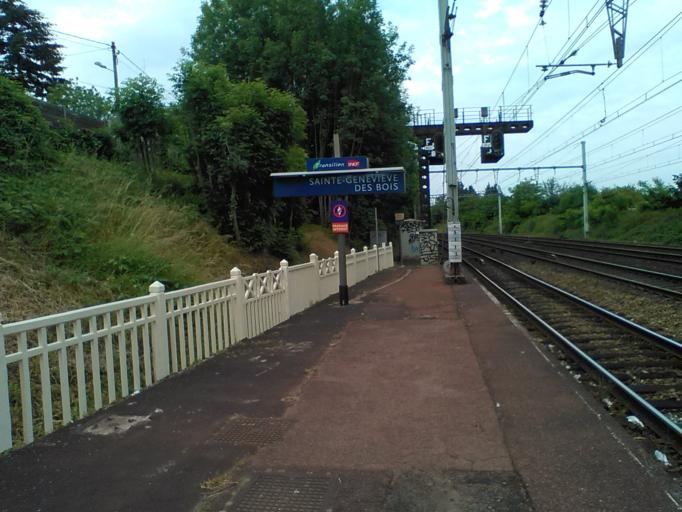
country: FR
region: Ile-de-France
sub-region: Departement de l'Essonne
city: Sainte-Genevieve-des-Bois
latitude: 48.6522
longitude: 2.3117
